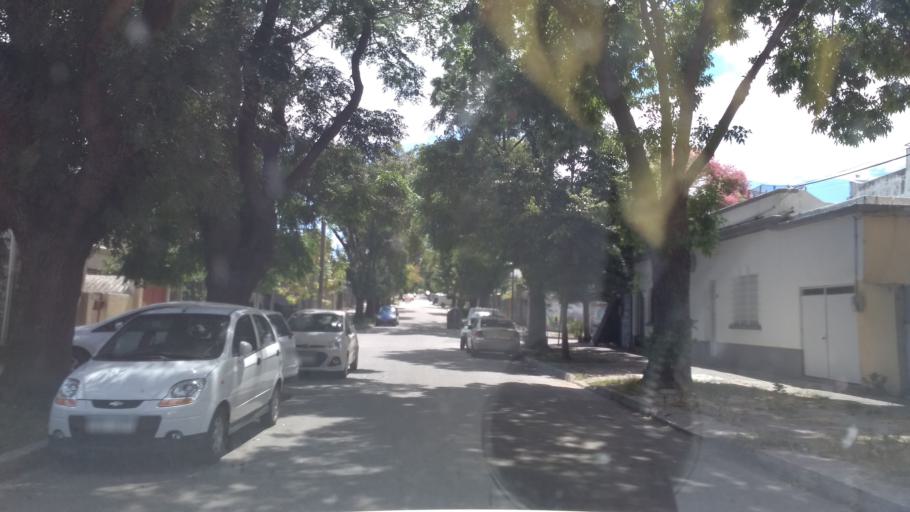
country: UY
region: Montevideo
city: Montevideo
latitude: -34.8923
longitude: -56.1216
